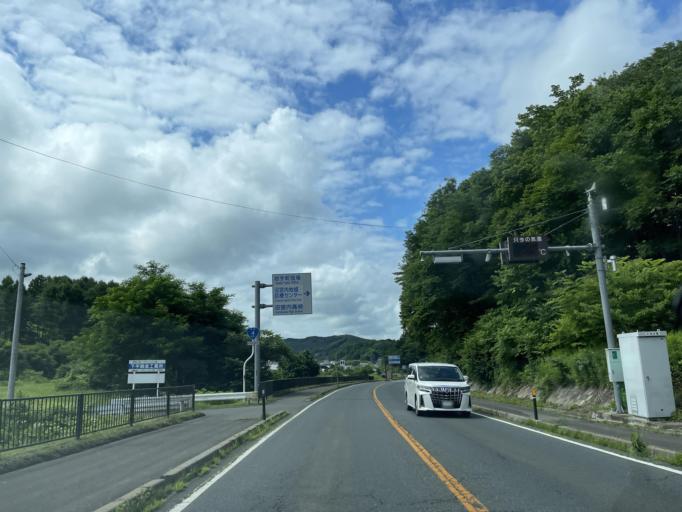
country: JP
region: Iwate
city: Ichinohe
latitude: 39.9715
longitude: 141.2142
